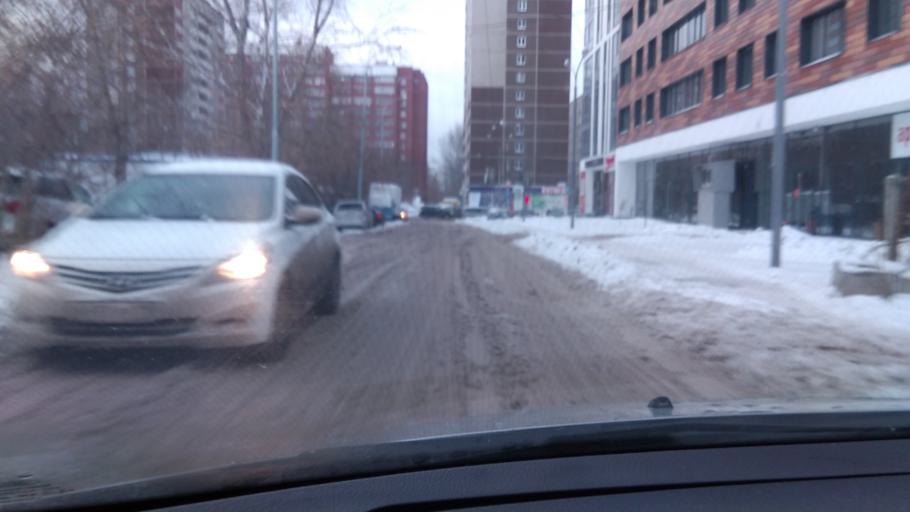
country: RU
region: Sverdlovsk
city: Yekaterinburg
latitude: 56.8061
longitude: 60.5962
